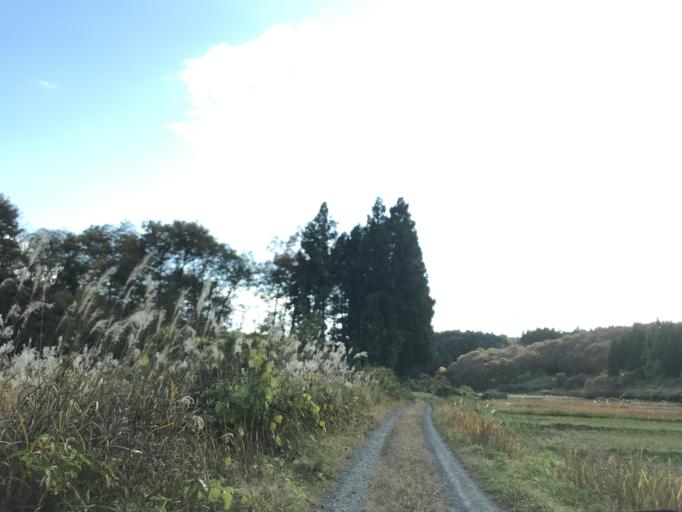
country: JP
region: Iwate
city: Ichinoseki
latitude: 38.8717
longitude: 141.1388
